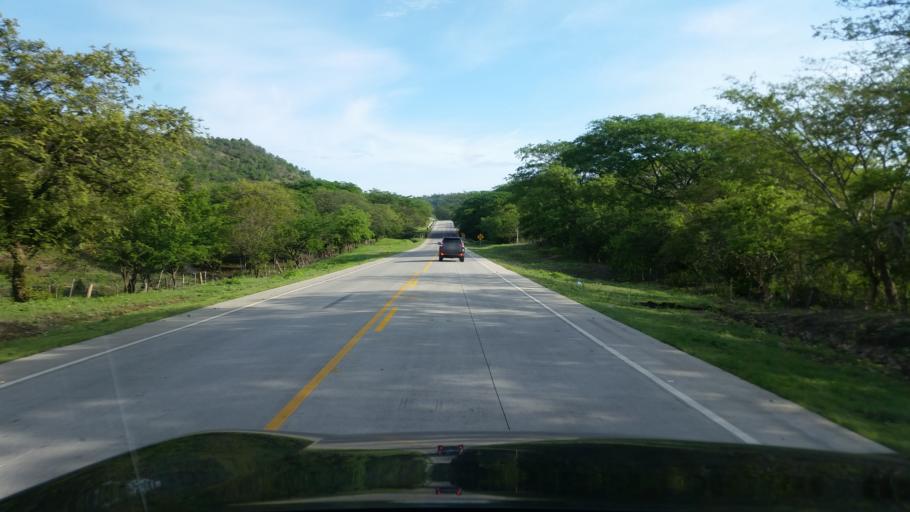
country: NI
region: Leon
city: Nagarote
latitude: 12.1493
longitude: -86.6530
